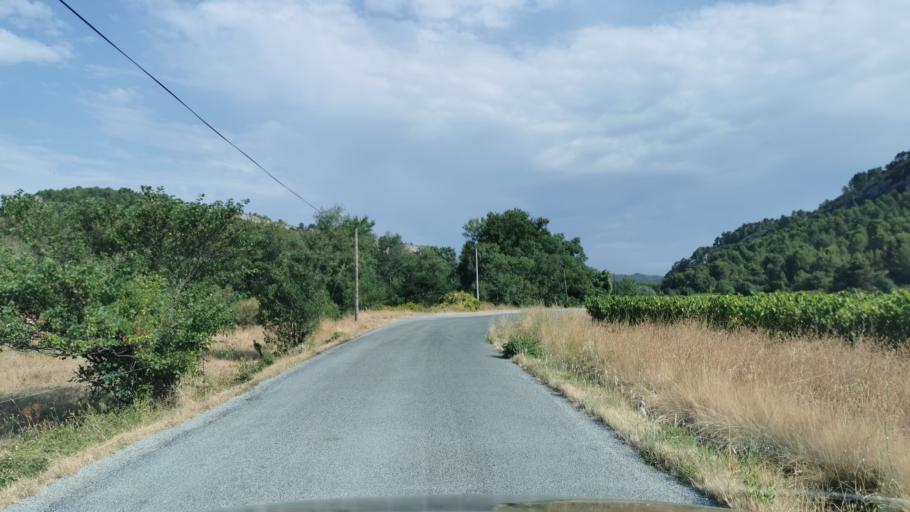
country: FR
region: Languedoc-Roussillon
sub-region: Departement de l'Aude
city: Bize-Minervois
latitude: 43.3261
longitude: 2.8790
